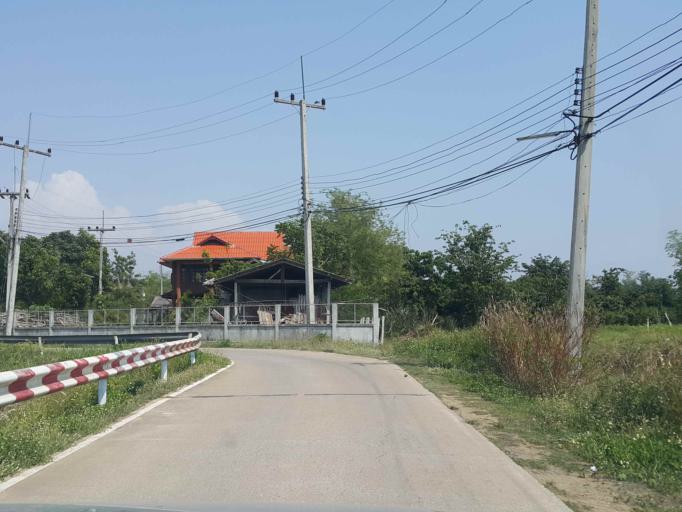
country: TH
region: Chiang Mai
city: San Kamphaeng
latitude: 18.7869
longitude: 99.1110
